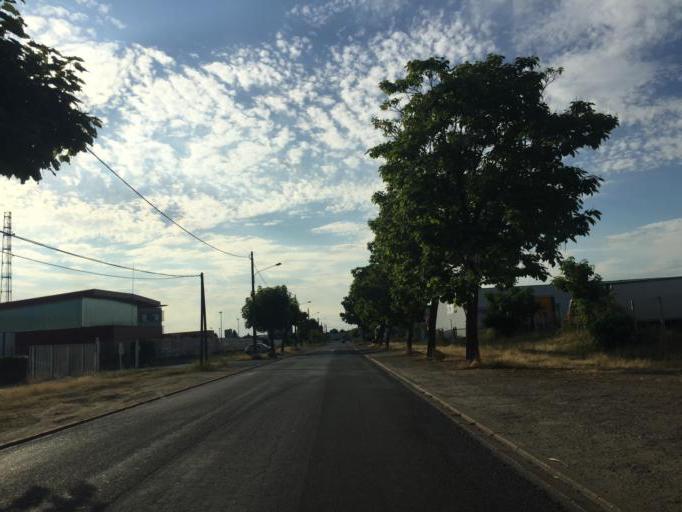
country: FR
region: Auvergne
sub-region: Departement de l'Allier
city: Yzeure
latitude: 46.5467
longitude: 3.3522
